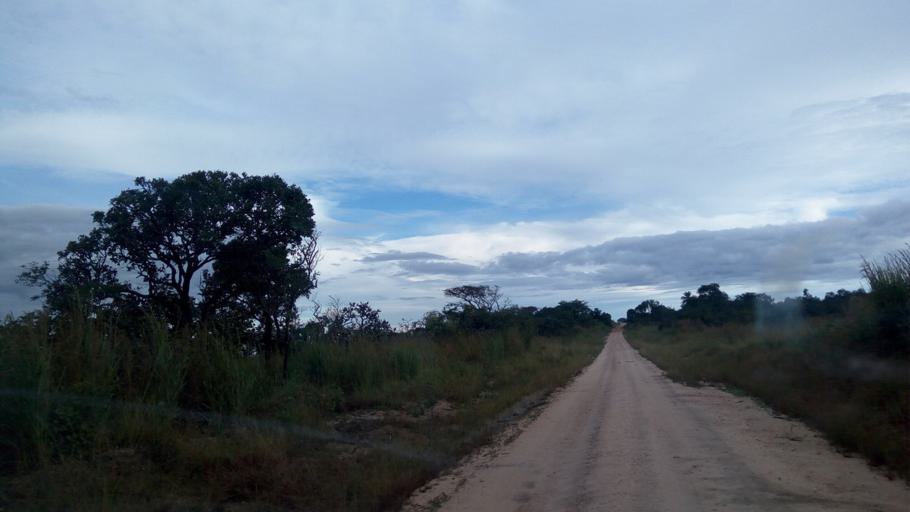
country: CD
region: Katanga
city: Kalemie
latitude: -6.5907
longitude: 29.0388
